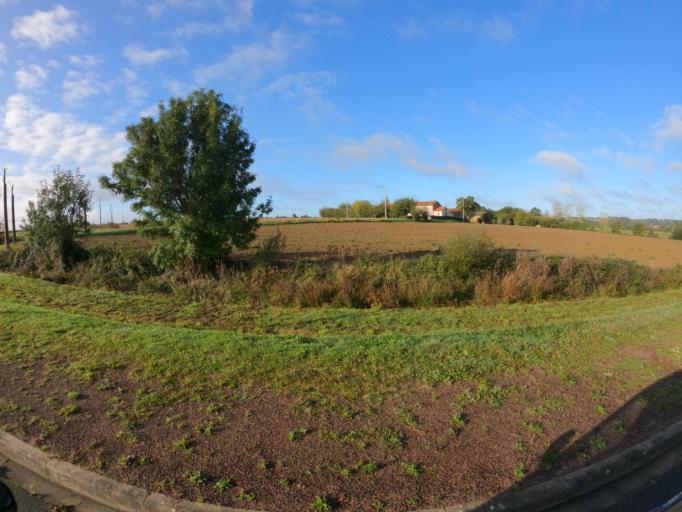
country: FR
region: Pays de la Loire
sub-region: Departement de Maine-et-Loire
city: La Seguiniere
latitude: 47.0565
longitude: -0.9448
